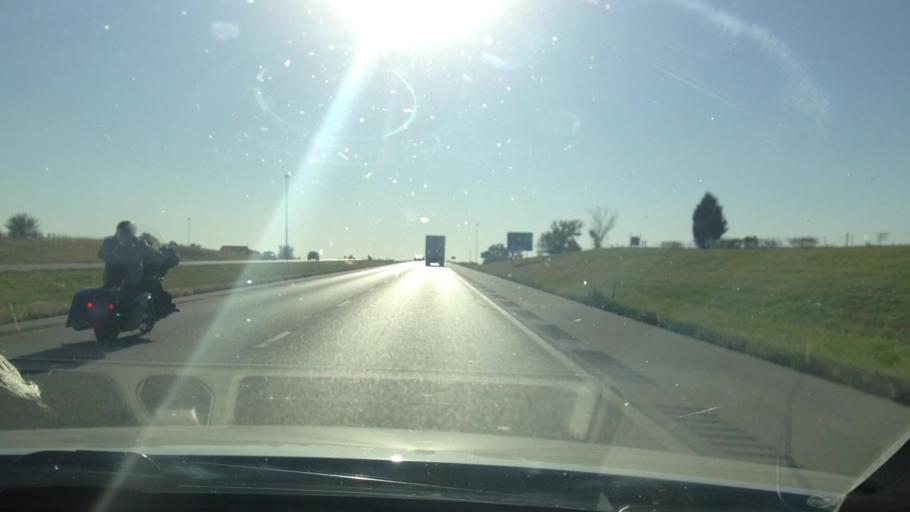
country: US
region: Kansas
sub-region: Johnson County
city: Gardner
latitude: 38.8163
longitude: -94.8734
